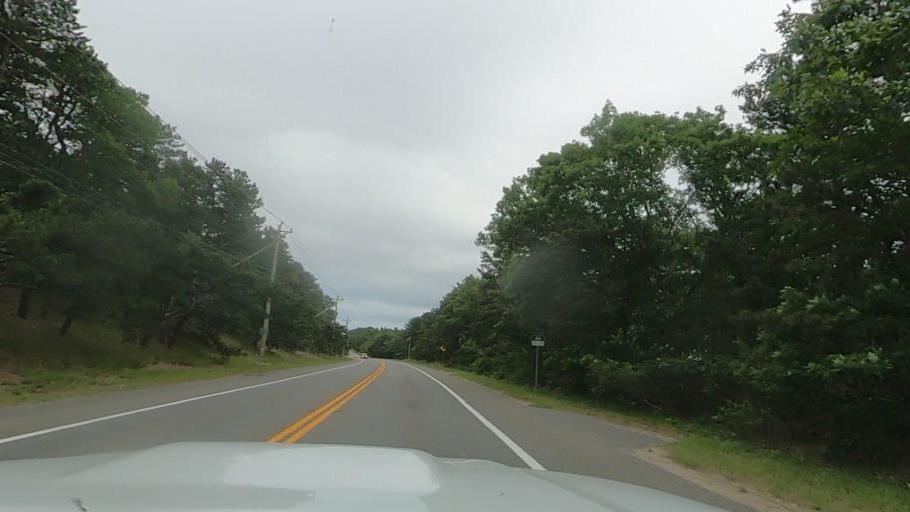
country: US
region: Massachusetts
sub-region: Barnstable County
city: Truro
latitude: 41.9797
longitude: -70.0419
